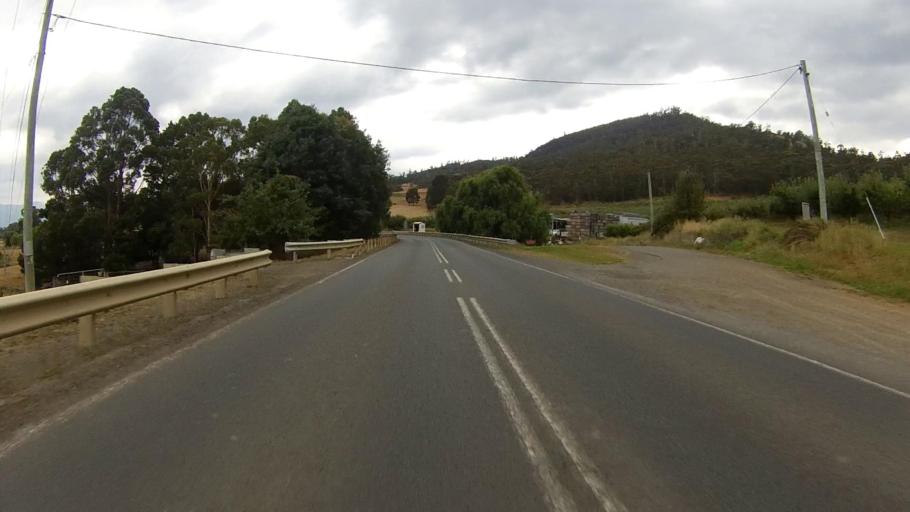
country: AU
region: Tasmania
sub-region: Huon Valley
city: Franklin
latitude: -43.0889
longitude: 147.0280
